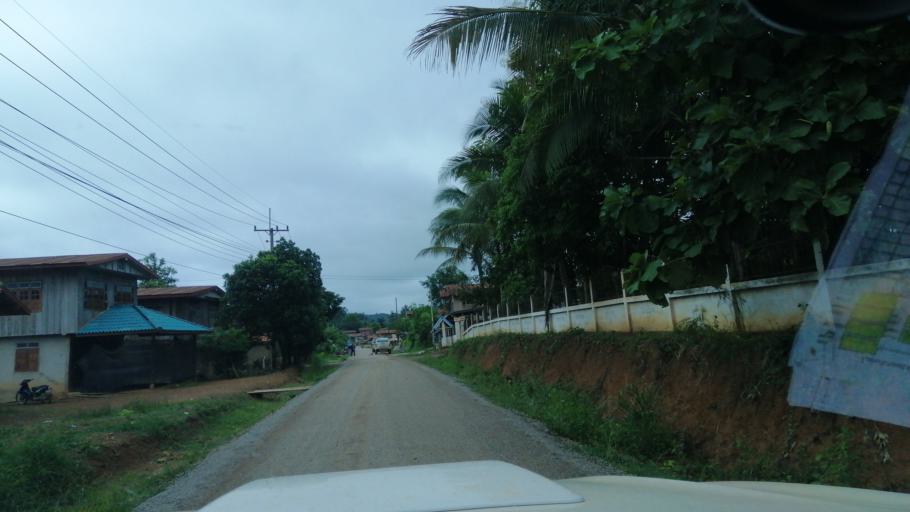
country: LA
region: Xiagnabouli
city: Muang Kenthao
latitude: 17.9464
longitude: 101.4054
